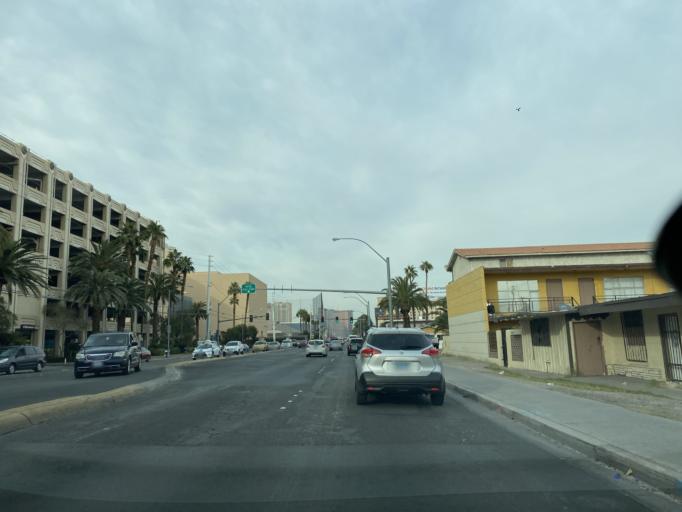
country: US
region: Nevada
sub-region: Clark County
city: Paradise
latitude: 36.1018
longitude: -115.1638
